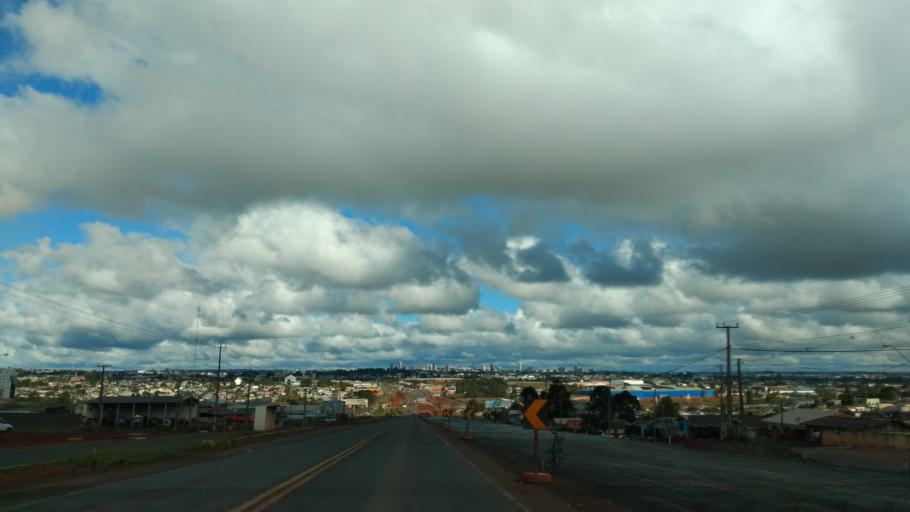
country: BR
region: Parana
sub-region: Guarapuava
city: Guarapuava
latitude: -25.3466
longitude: -51.4893
